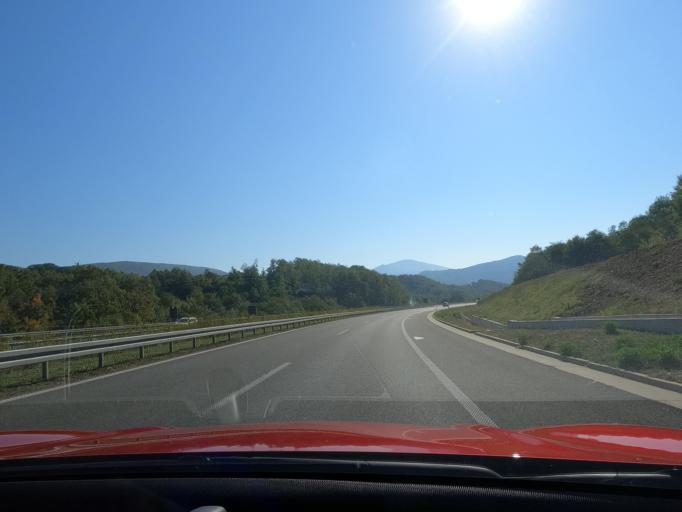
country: RS
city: Prislonica
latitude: 44.0111
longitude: 20.3783
